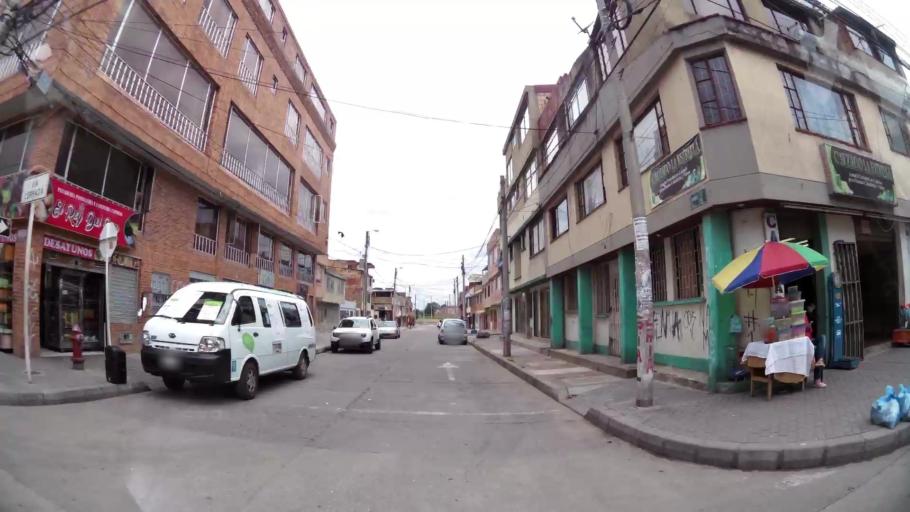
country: CO
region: Cundinamarca
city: Cota
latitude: 4.7651
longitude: -74.0360
